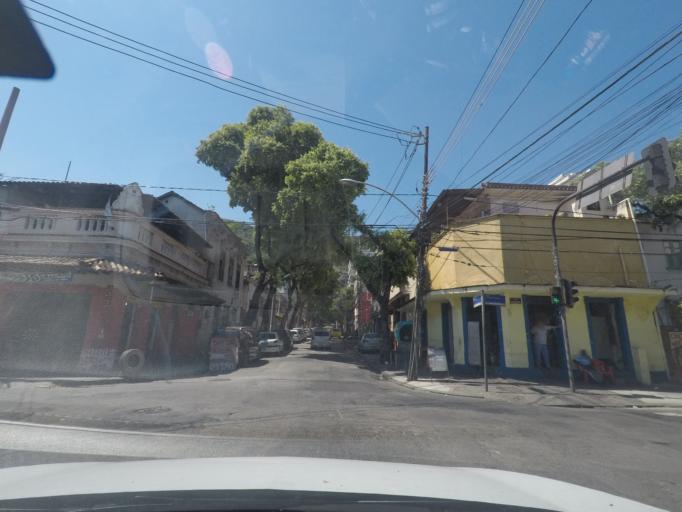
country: BR
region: Rio de Janeiro
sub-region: Rio De Janeiro
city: Rio de Janeiro
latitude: -22.9148
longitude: -43.2506
